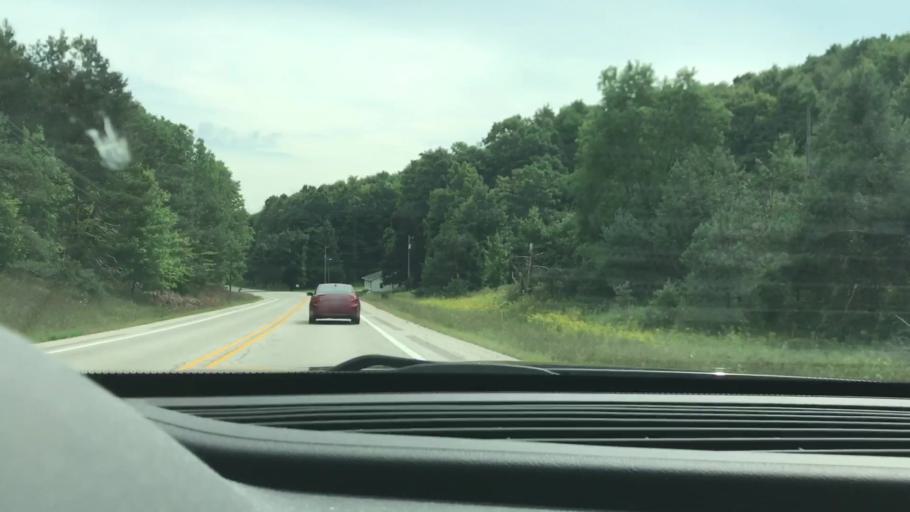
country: US
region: Michigan
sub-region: Antrim County
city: Bellaire
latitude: 45.0835
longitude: -85.2857
